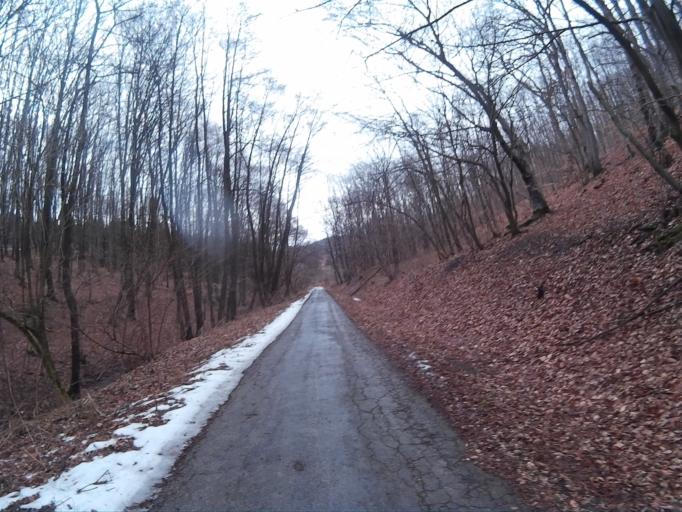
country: HU
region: Heves
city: Belapatfalva
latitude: 48.0601
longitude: 20.3816
